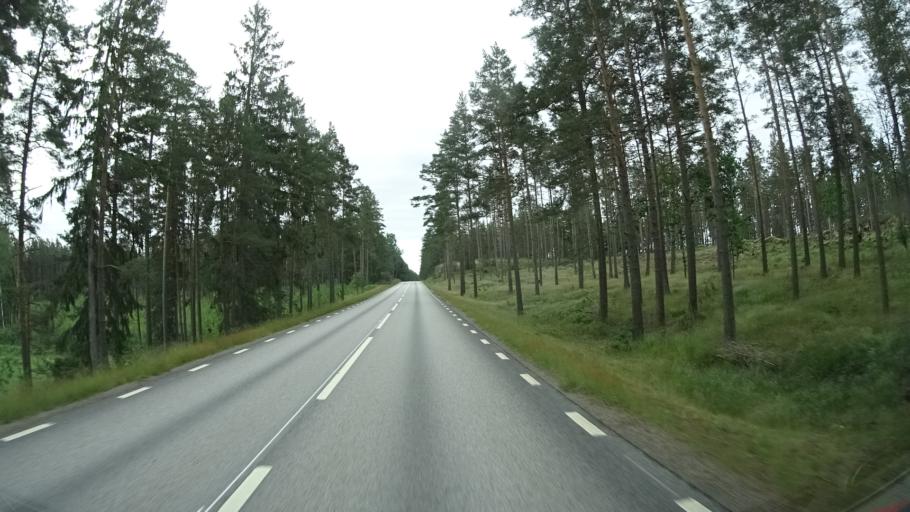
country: SE
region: Kalmar
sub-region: Oskarshamns Kommun
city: Oskarshamn
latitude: 57.2691
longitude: 16.3106
